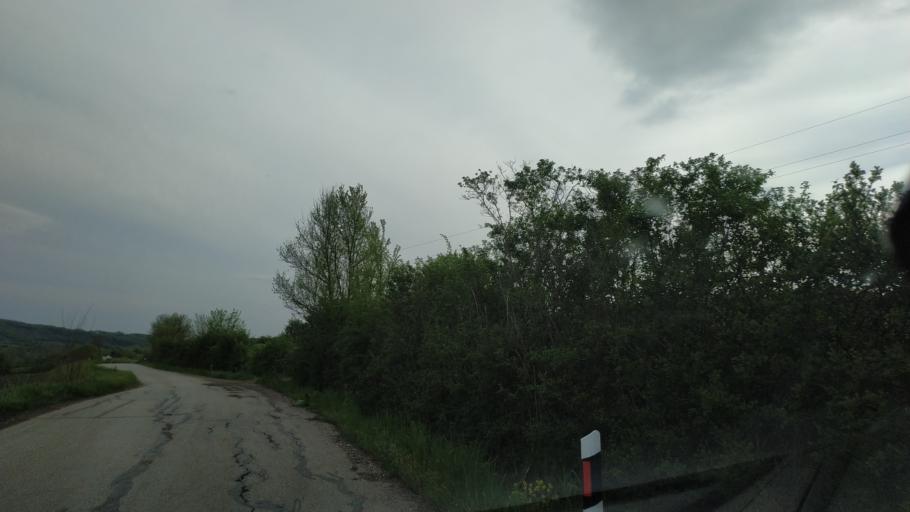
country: RS
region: Central Serbia
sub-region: Zajecarski Okrug
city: Soko Banja
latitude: 43.5145
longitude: 21.8449
